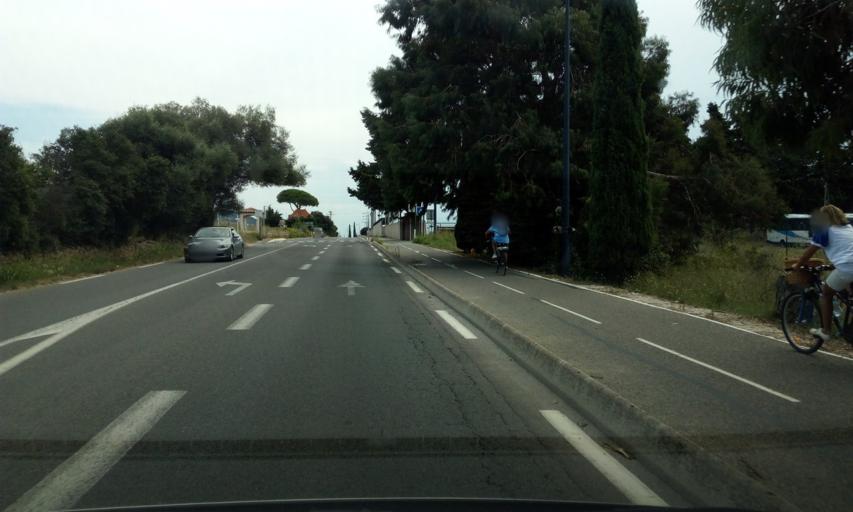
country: FR
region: Provence-Alpes-Cote d'Azur
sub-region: Departement du Var
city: Carqueiranne
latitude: 43.1012
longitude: 6.0590
